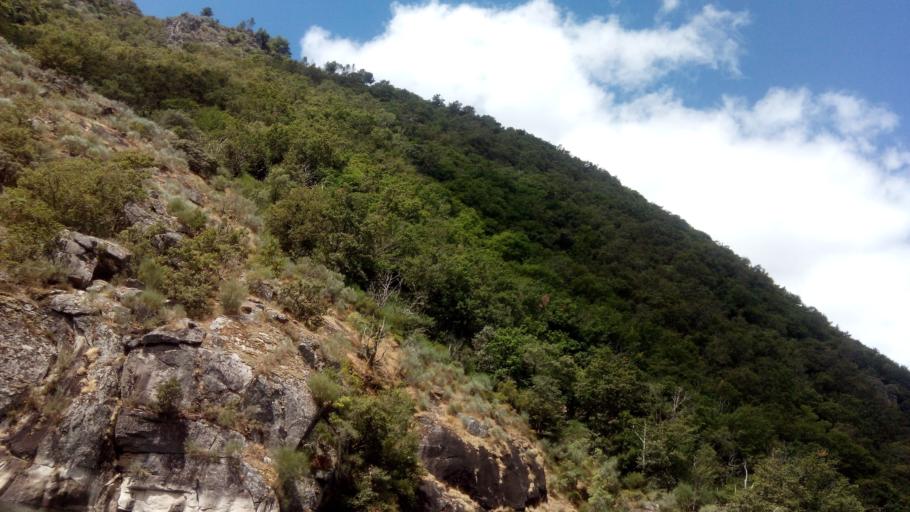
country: ES
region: Galicia
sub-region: Provincia de Lugo
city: Sober
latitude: 42.4001
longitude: -7.6291
